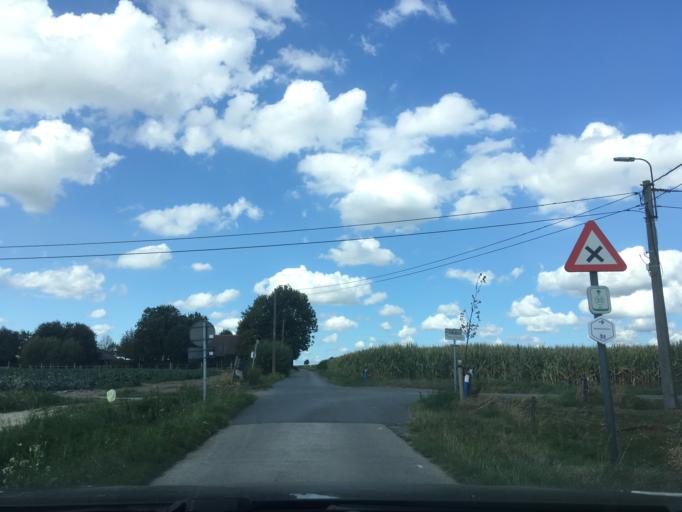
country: BE
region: Flanders
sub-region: Provincie West-Vlaanderen
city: Staden
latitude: 50.9522
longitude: 3.0510
